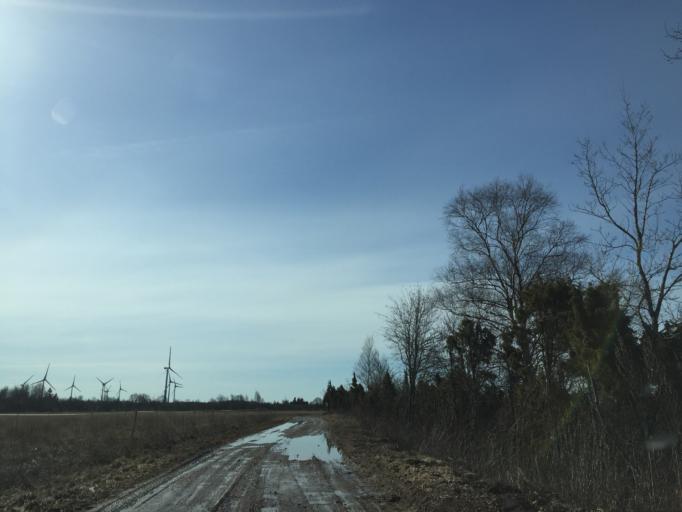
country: EE
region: Laeaene
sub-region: Haapsalu linn
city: Haapsalu
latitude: 58.6523
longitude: 23.5135
